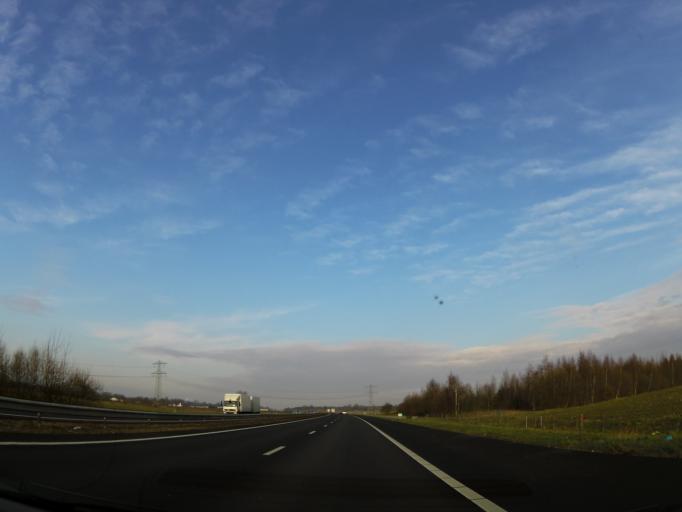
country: NL
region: Limburg
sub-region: Gemeente Venlo
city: Arcen
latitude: 51.4321
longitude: 6.1023
